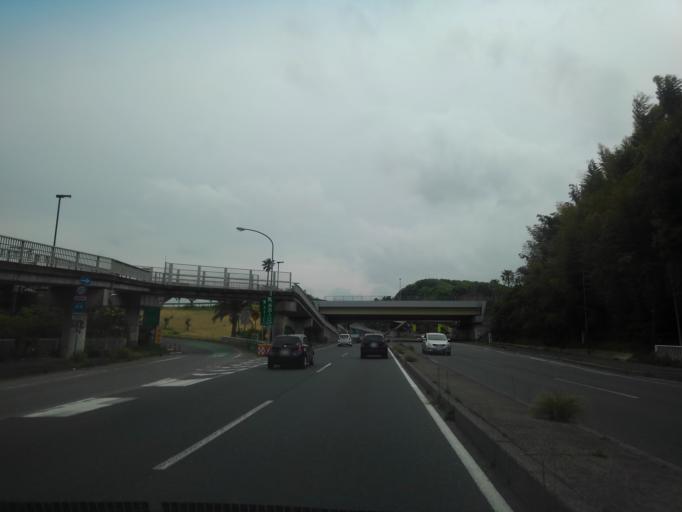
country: JP
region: Chiba
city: Kisarazu
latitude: 35.3513
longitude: 139.9204
